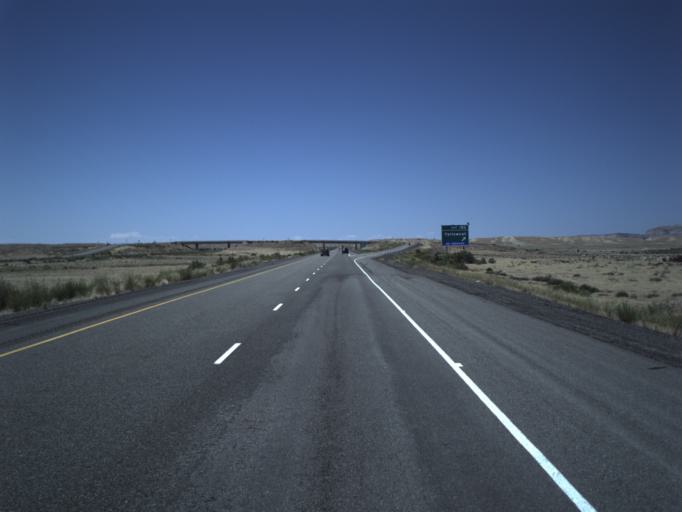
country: US
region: Utah
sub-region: Grand County
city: Moab
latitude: 38.9428
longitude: -109.6062
